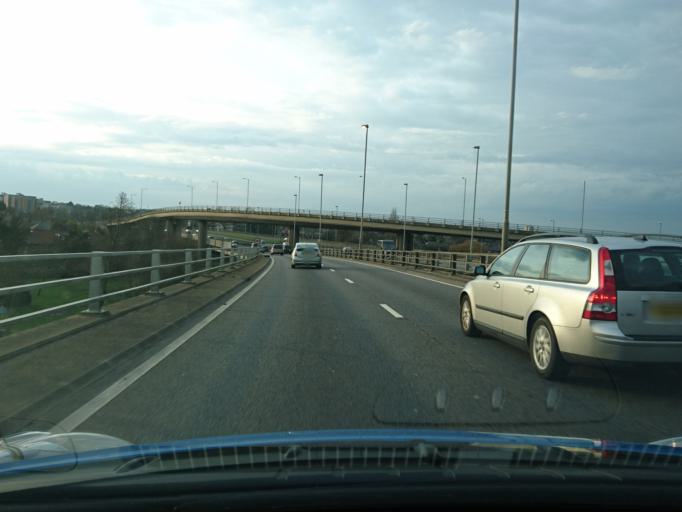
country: GB
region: England
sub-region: Greater London
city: Woodford Green
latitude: 51.5929
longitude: 0.0362
